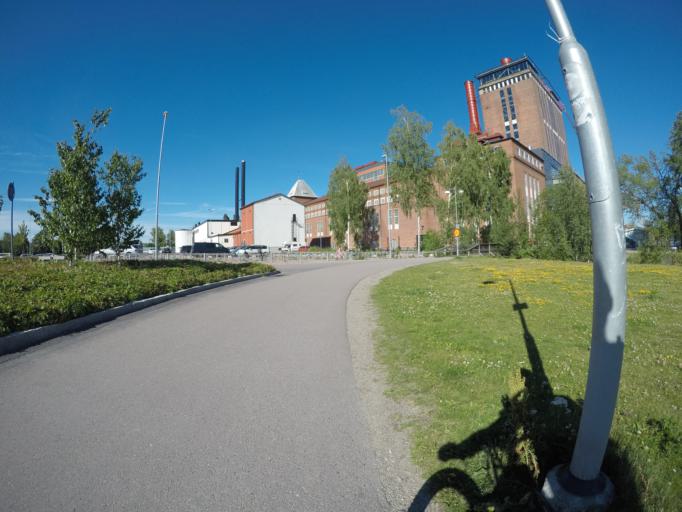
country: SE
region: Vaestmanland
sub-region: Vasteras
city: Vasteras
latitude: 59.6069
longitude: 16.5654
